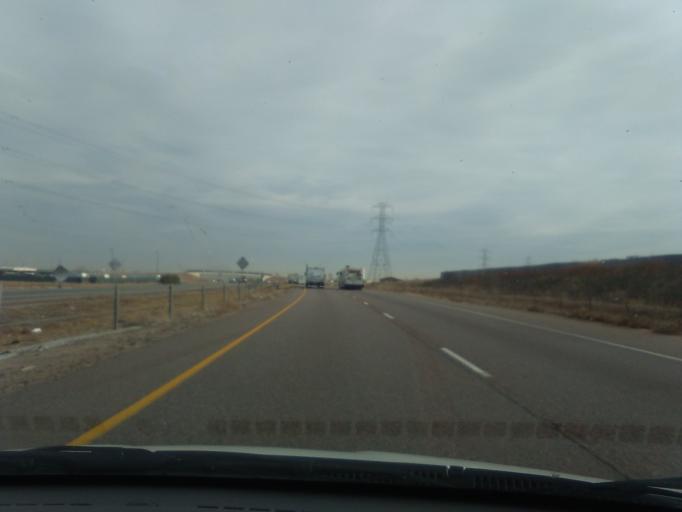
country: US
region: Colorado
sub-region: Adams County
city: Derby
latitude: 39.8820
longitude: -104.8749
